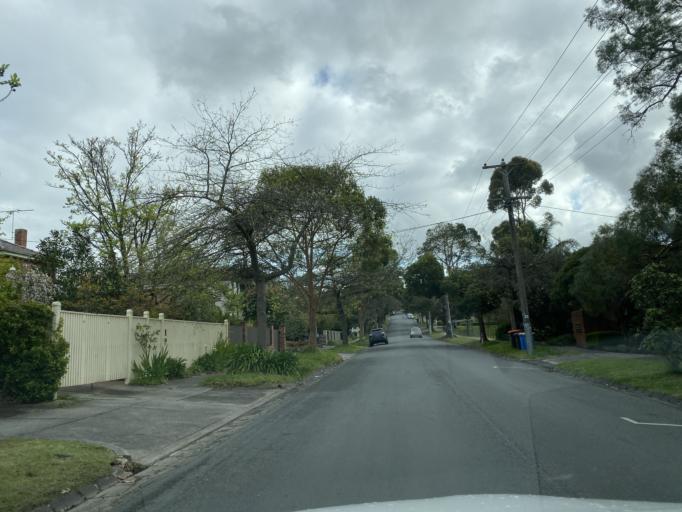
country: AU
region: Victoria
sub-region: Boroondara
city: Canterbury
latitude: -37.8341
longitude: 145.0912
